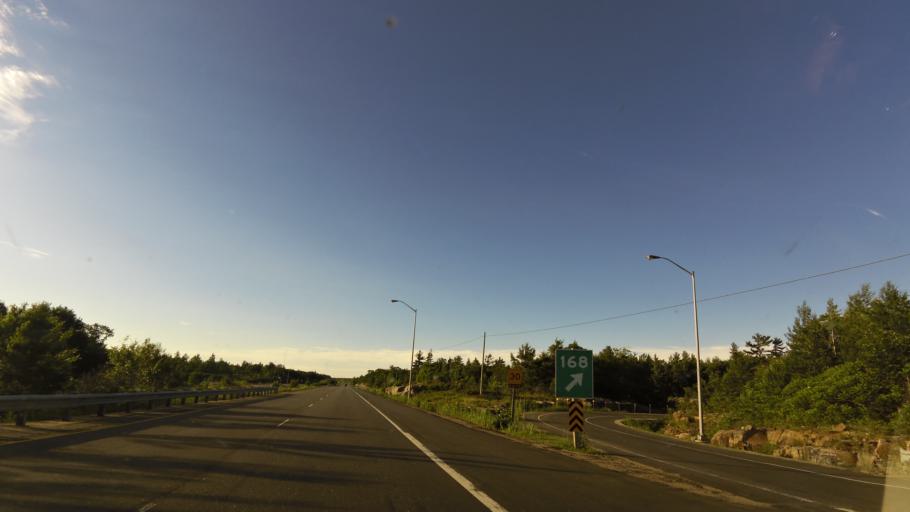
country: CA
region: Ontario
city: Midland
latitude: 44.9185
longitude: -79.7751
